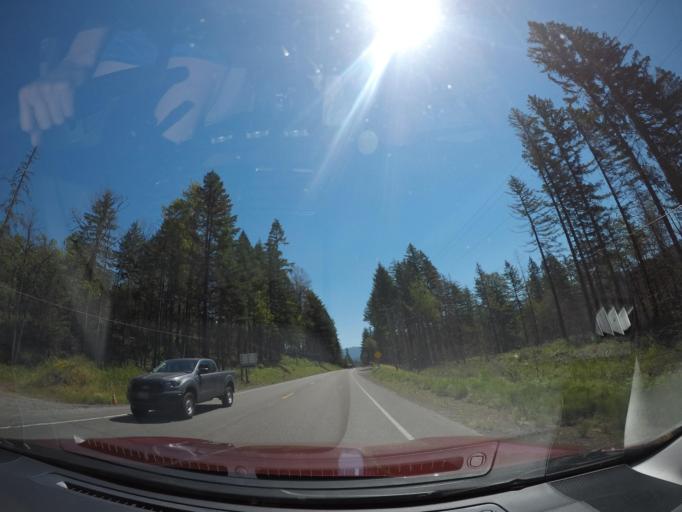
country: US
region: Oregon
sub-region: Linn County
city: Mill City
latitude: 44.7570
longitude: -122.4344
